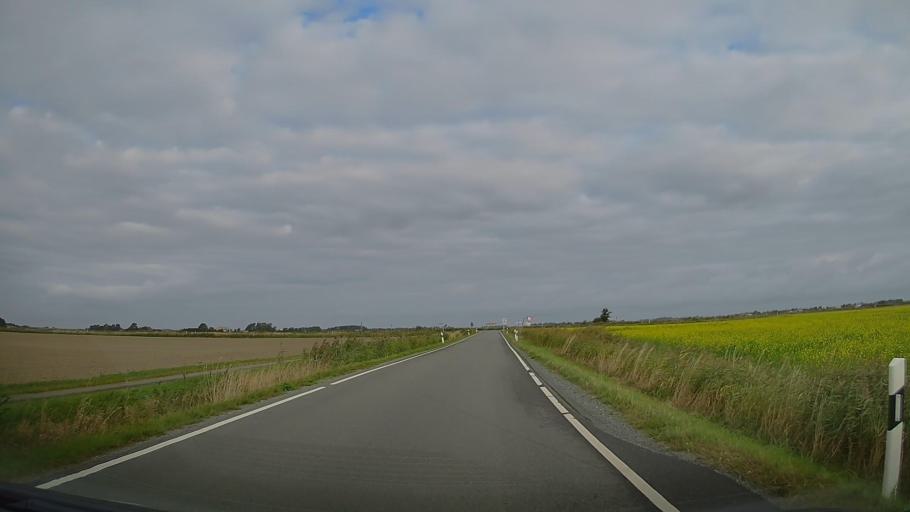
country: DE
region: Schleswig-Holstein
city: Ockholm
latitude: 54.6637
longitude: 8.8360
